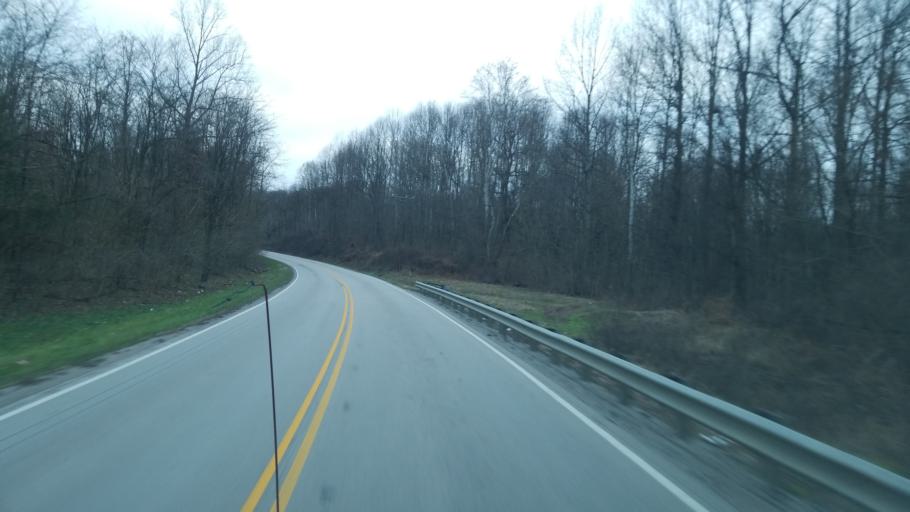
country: US
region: Ohio
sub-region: Brown County
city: Aberdeen
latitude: 38.6884
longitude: -83.7912
